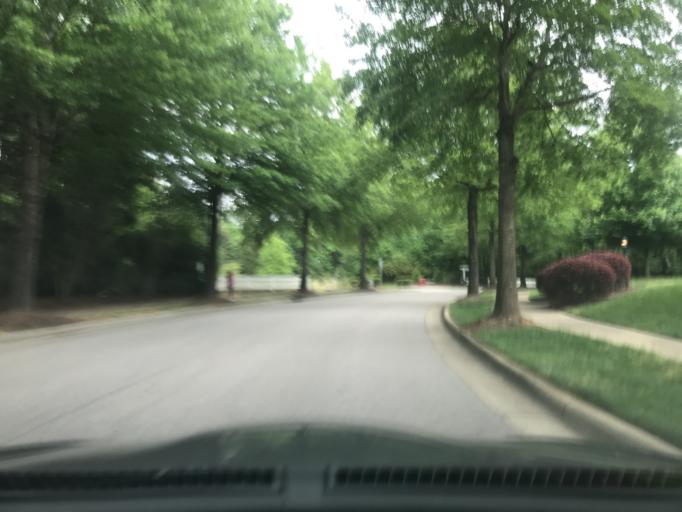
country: US
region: North Carolina
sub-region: Wake County
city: Wake Forest
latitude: 35.9290
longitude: -78.5599
